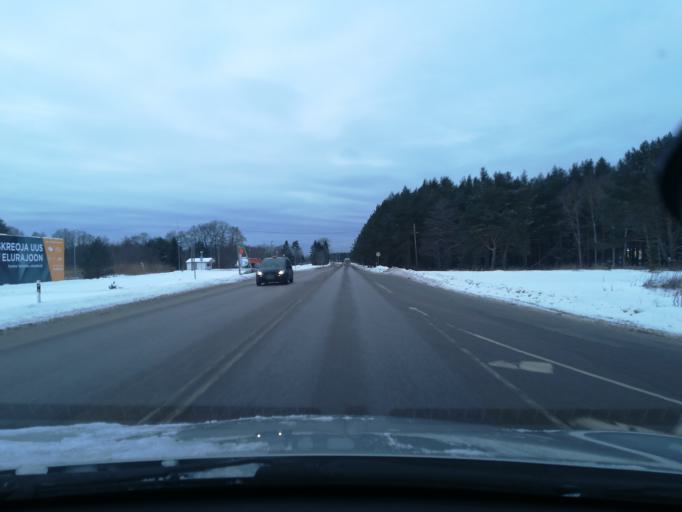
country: EE
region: Harju
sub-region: Harku vald
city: Tabasalu
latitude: 59.4337
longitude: 24.5901
